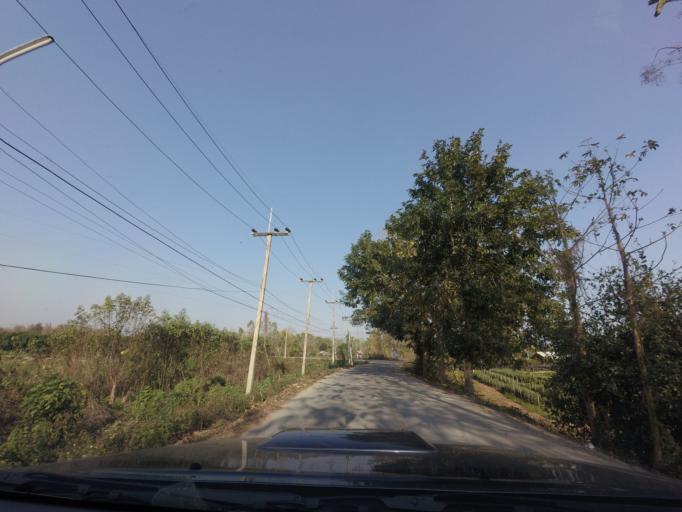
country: TH
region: Chiang Mai
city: San Sai
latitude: 18.9321
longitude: 98.9683
